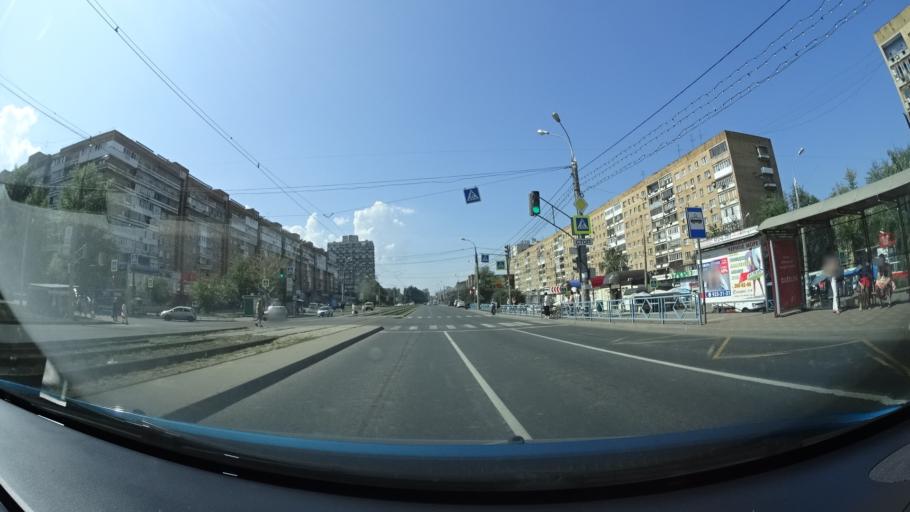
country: RU
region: Samara
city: Samara
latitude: 53.2106
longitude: 50.1412
